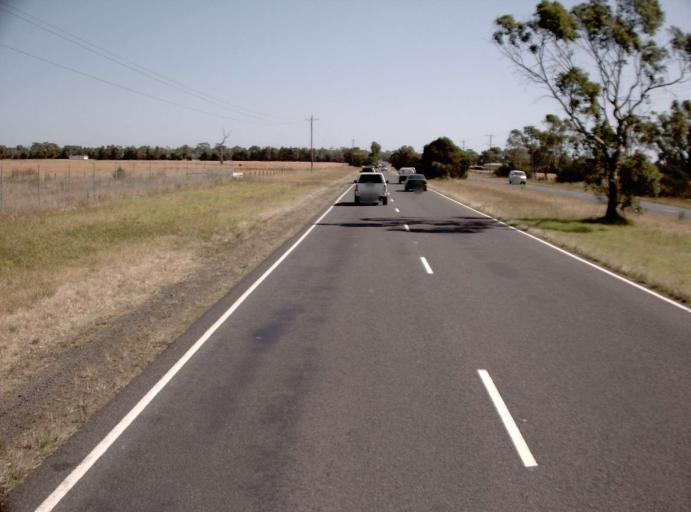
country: AU
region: Victoria
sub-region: Frankston
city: Sandhurst
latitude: -38.0794
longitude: 145.1889
